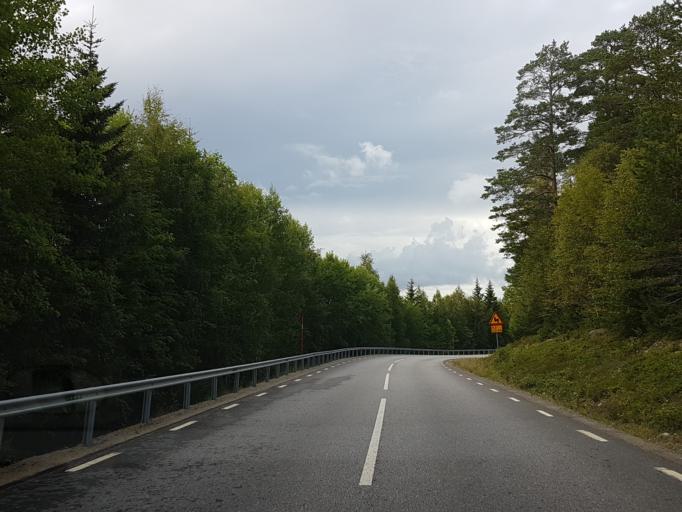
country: SE
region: Vaesterbotten
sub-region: Umea Kommun
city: Holmsund
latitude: 63.7780
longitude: 20.3870
